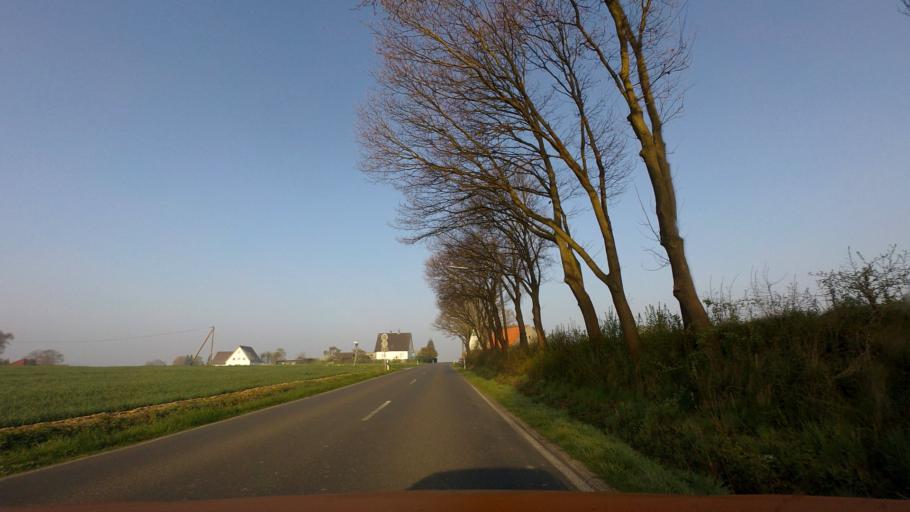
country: DE
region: North Rhine-Westphalia
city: Enger
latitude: 52.1508
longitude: 8.5323
